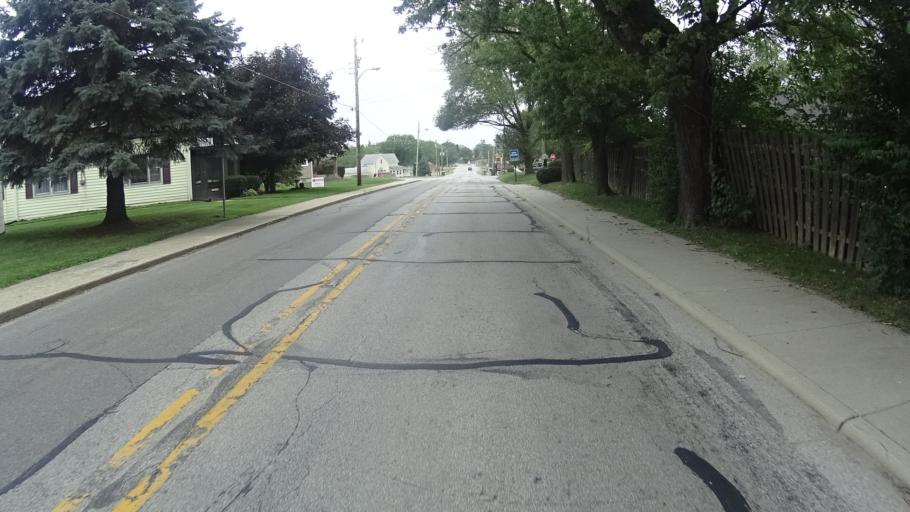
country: US
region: Indiana
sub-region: Madison County
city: Lapel
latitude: 40.0688
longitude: -85.8526
